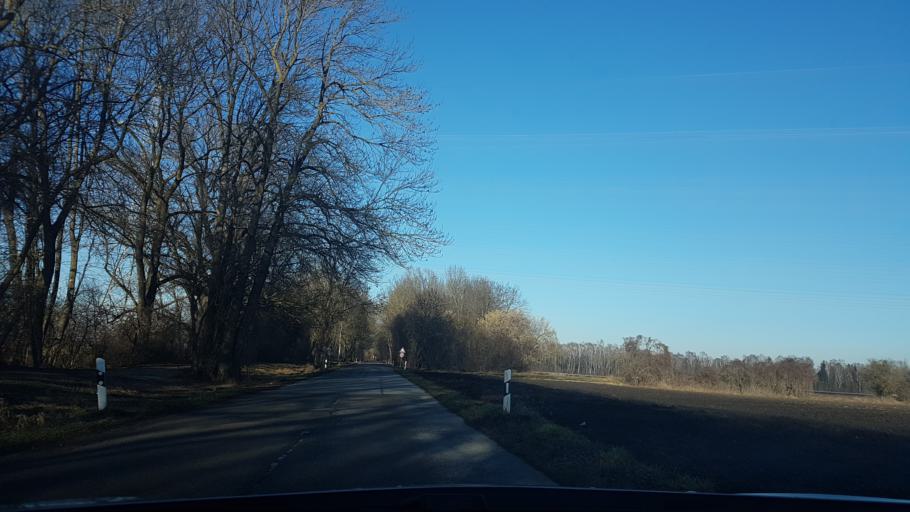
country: DE
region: Bavaria
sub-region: Upper Bavaria
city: Eichenried
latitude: 48.2773
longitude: 11.7517
